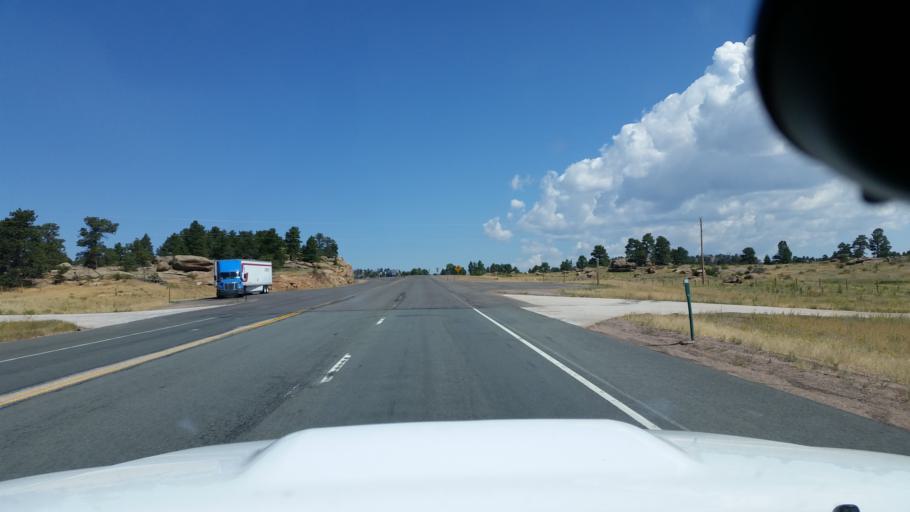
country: US
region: Wyoming
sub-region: Albany County
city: Laramie
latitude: 40.9974
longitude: -105.4126
